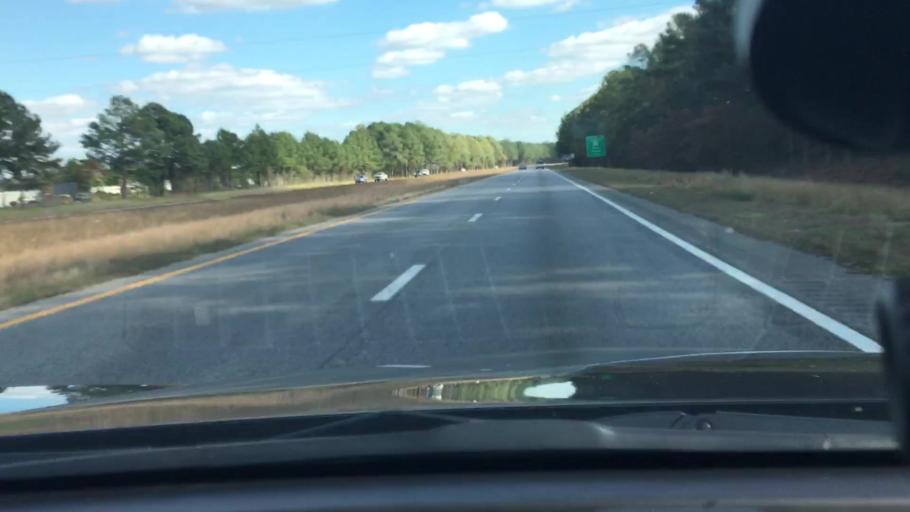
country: US
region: North Carolina
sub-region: Wilson County
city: Lucama
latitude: 35.7719
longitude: -78.0485
